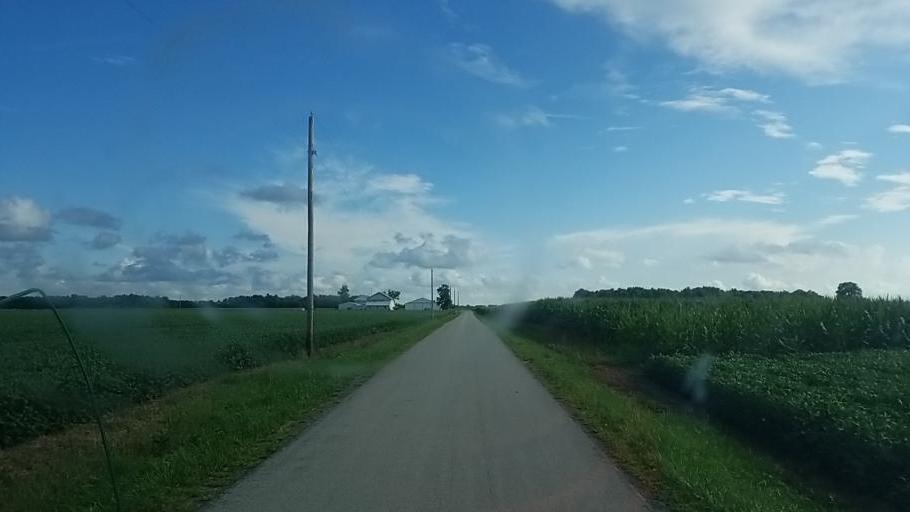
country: US
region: Ohio
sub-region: Wyandot County
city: Upper Sandusky
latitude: 40.7776
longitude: -83.3810
